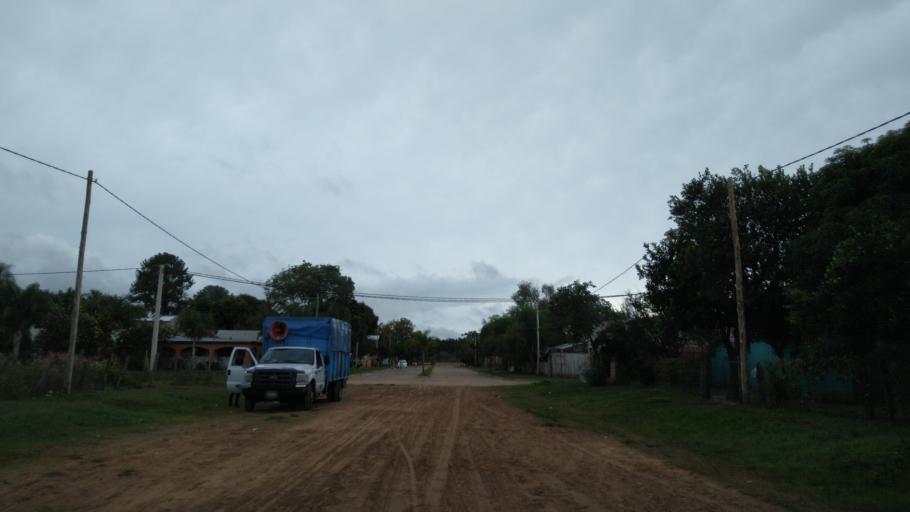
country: AR
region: Corrientes
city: Ituzaingo
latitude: -27.6326
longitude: -56.9086
